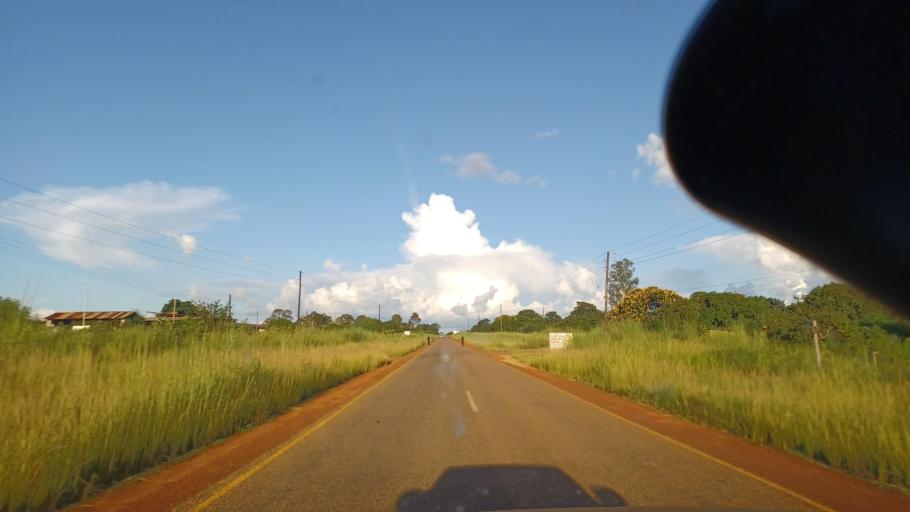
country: ZM
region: North-Western
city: Kalengwa
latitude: -13.1432
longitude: 25.0377
